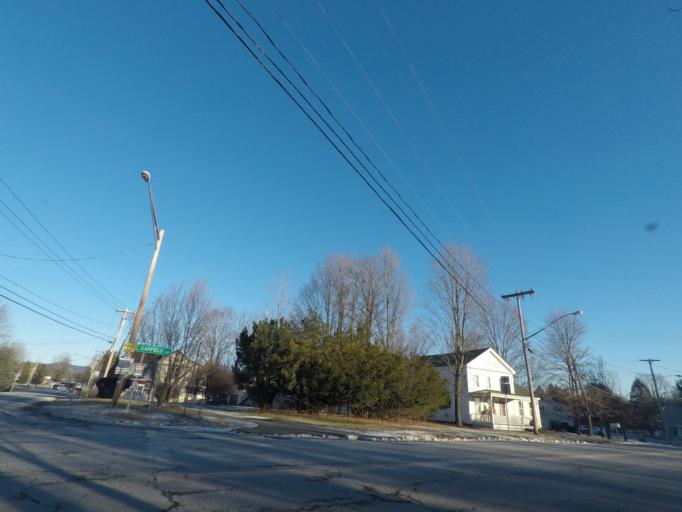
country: US
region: New York
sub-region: Rensselaer County
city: Poestenkill
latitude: 42.7292
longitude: -73.6003
